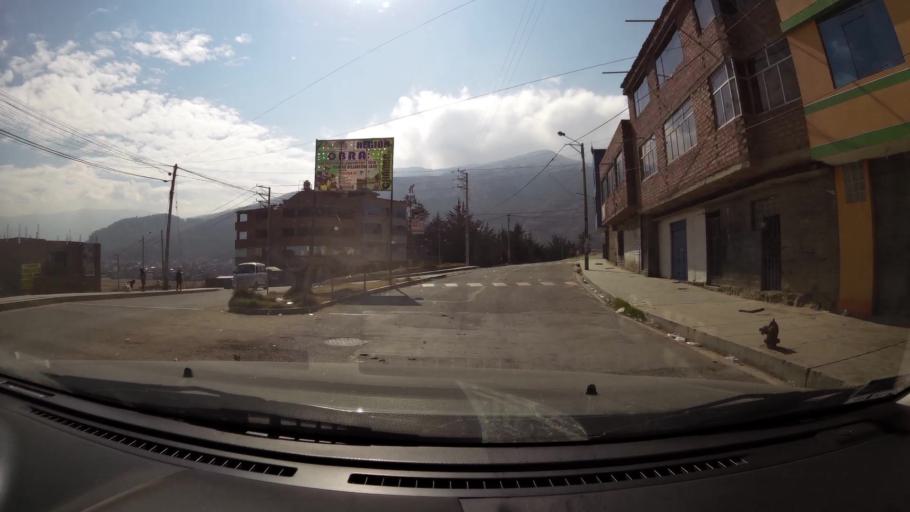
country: PE
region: Junin
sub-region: Provincia de Huancayo
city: Huancayo
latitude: -12.0578
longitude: -75.1941
